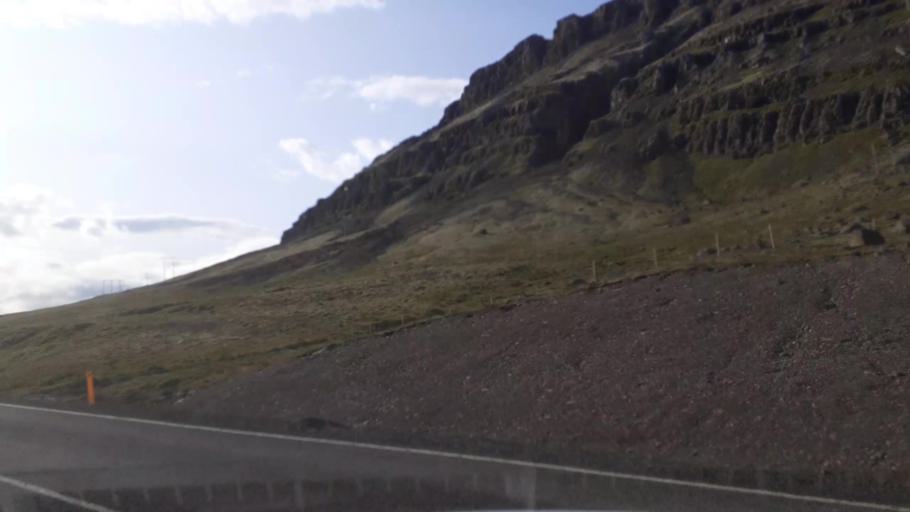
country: IS
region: East
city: Reydarfjoerdur
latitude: 64.7856
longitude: -14.4925
